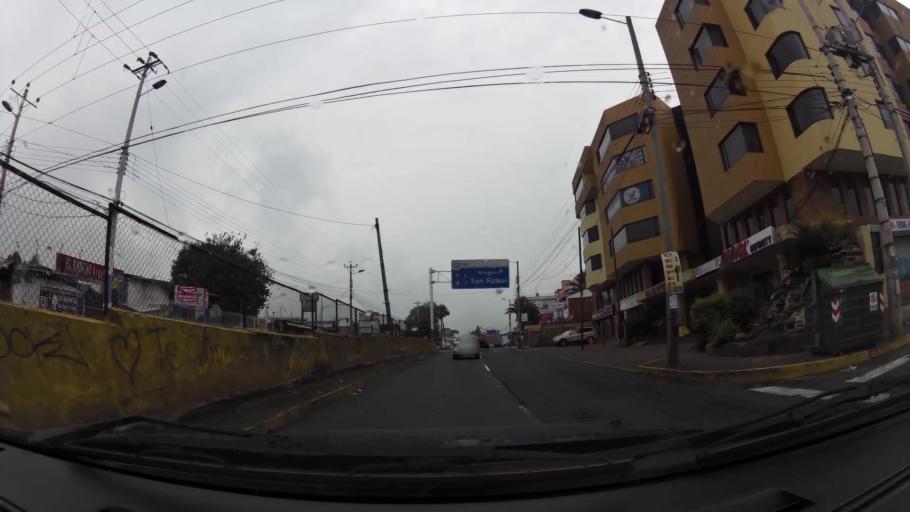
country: EC
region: Pichincha
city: Sangolqui
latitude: -0.2958
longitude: -78.4619
